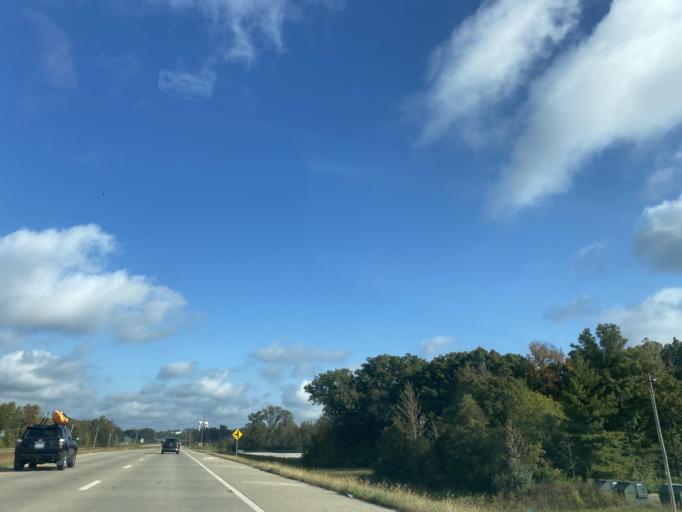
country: US
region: Kentucky
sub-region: Campbell County
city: Claryville
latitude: 38.8881
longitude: -84.3864
